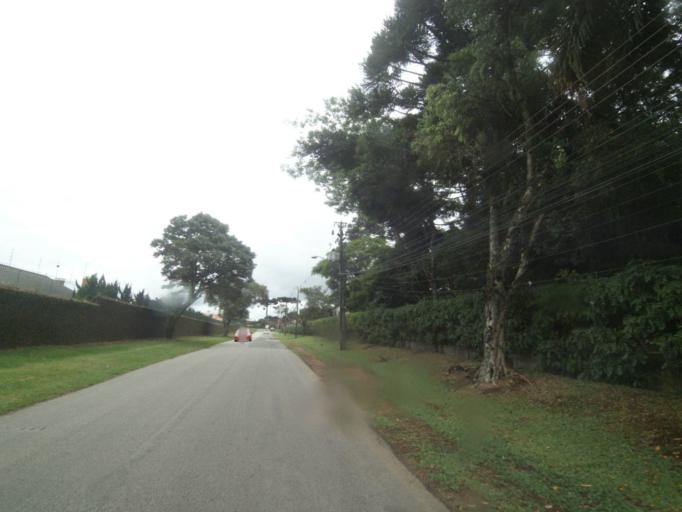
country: BR
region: Parana
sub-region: Curitiba
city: Curitiba
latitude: -25.4586
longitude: -49.3339
